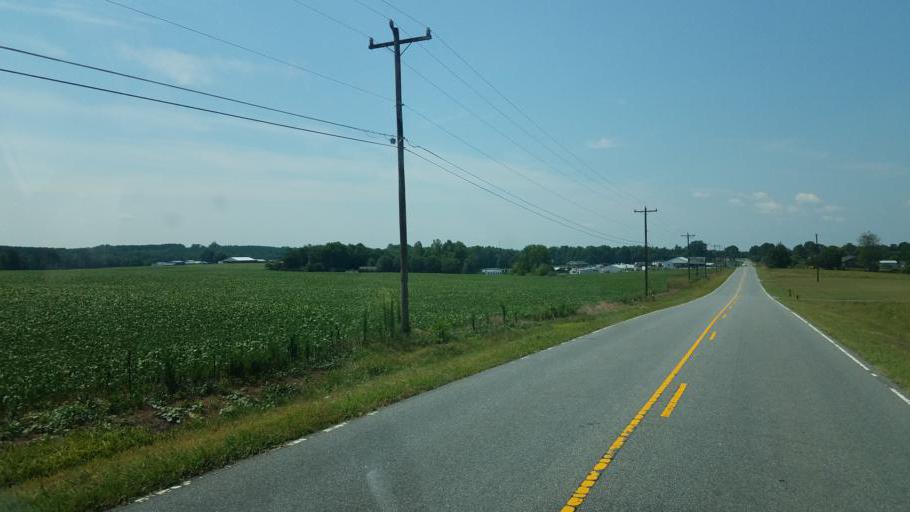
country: US
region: North Carolina
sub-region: Burke County
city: Icard
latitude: 35.5419
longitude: -81.5064
